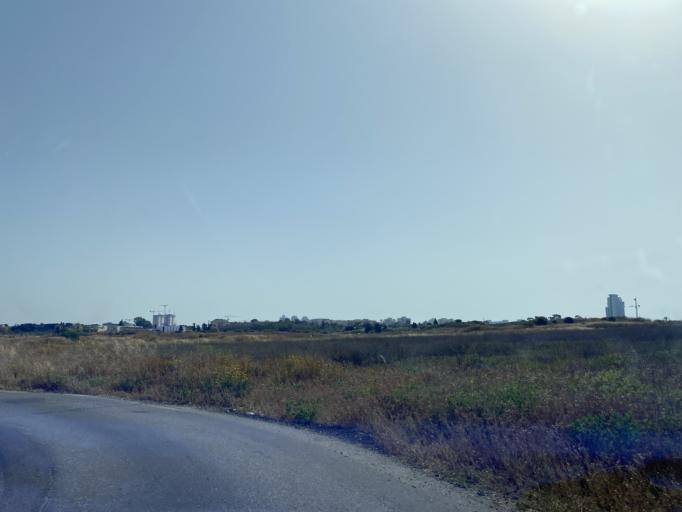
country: IL
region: Central District
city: Netanya
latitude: 32.3076
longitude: 34.8625
